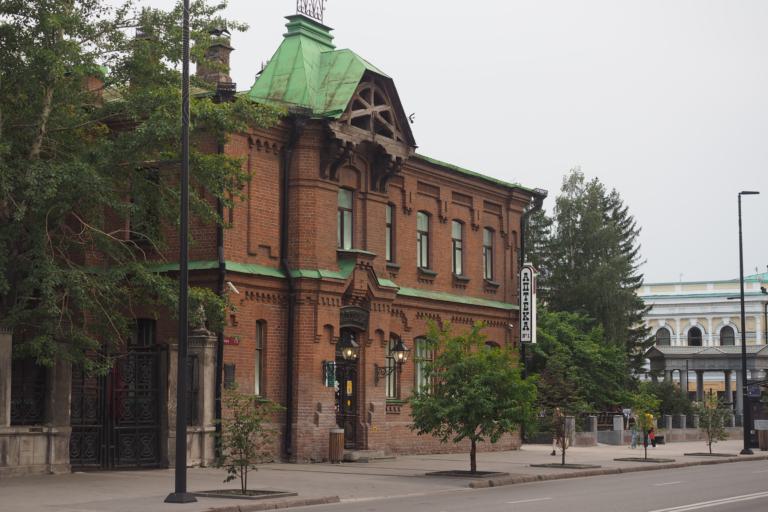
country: RU
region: Krasnoyarskiy
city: Krasnoyarsk
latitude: 56.0118
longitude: 92.8651
